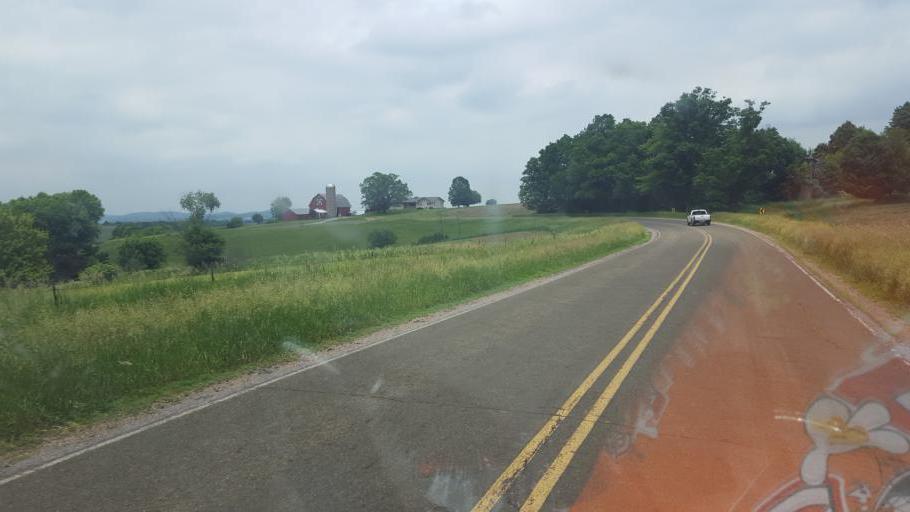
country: US
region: Wisconsin
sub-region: Vernon County
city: Hillsboro
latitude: 43.6492
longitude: -90.2930
